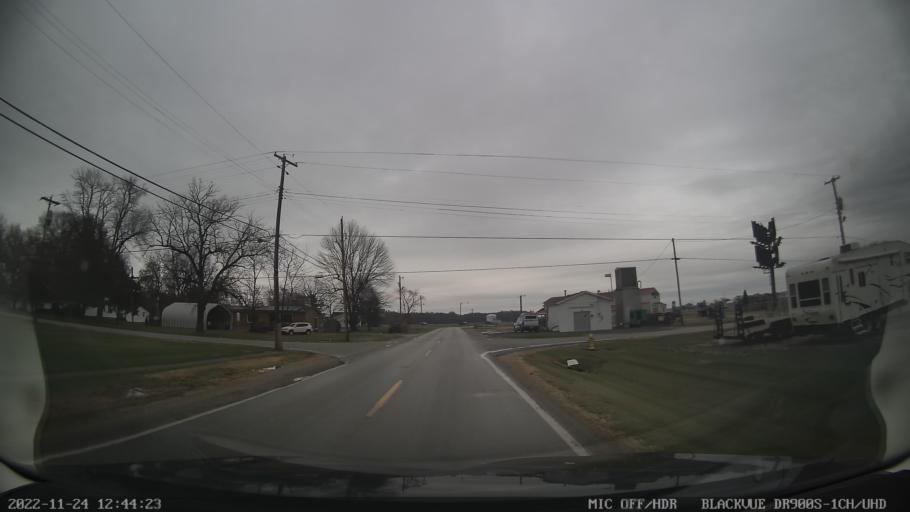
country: US
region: Illinois
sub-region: Macoupin County
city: Staunton
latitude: 38.9613
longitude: -89.7647
